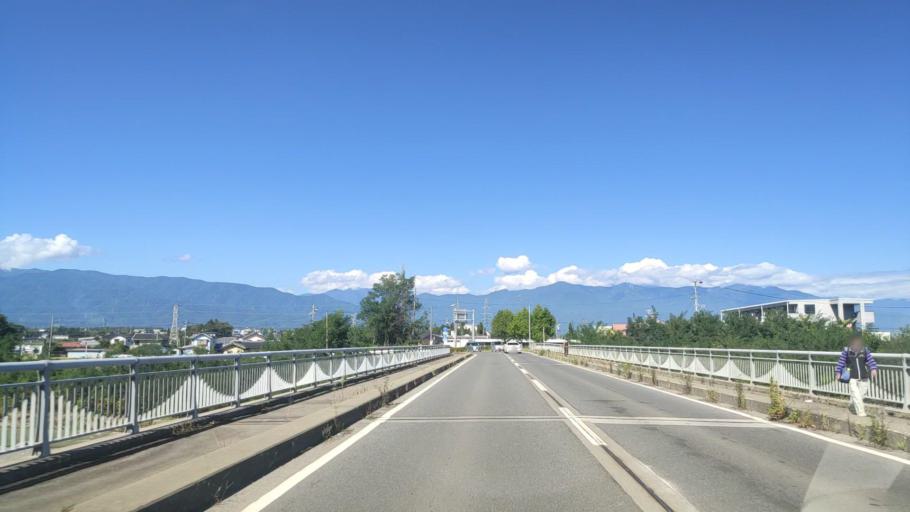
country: JP
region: Nagano
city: Shiojiri
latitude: 36.1642
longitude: 137.9446
